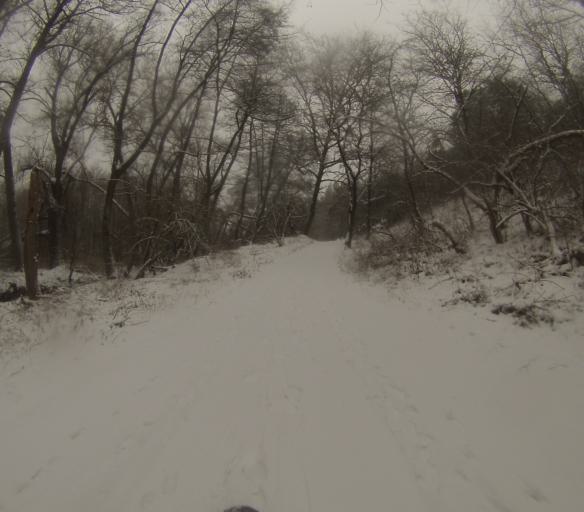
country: CZ
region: South Moravian
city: Orechov
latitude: 49.1293
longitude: 16.5414
